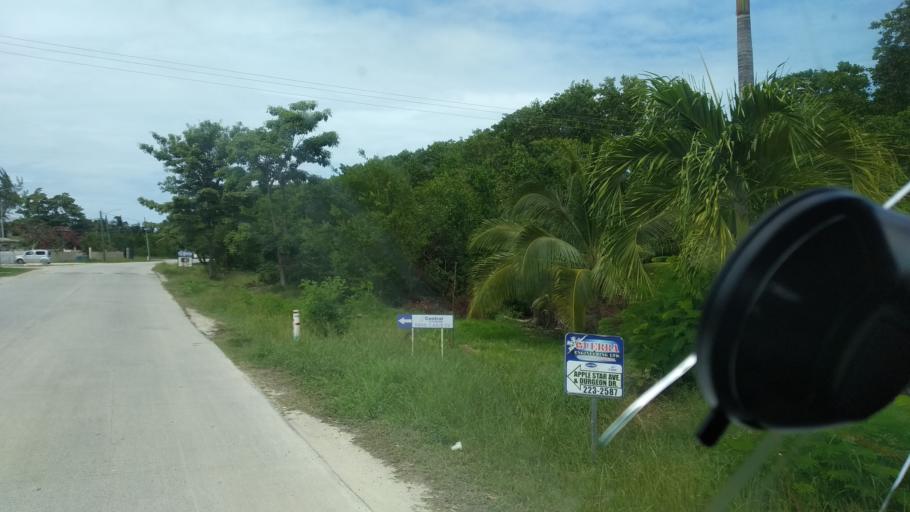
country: BZ
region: Belize
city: Belize City
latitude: 17.5123
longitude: -88.2004
